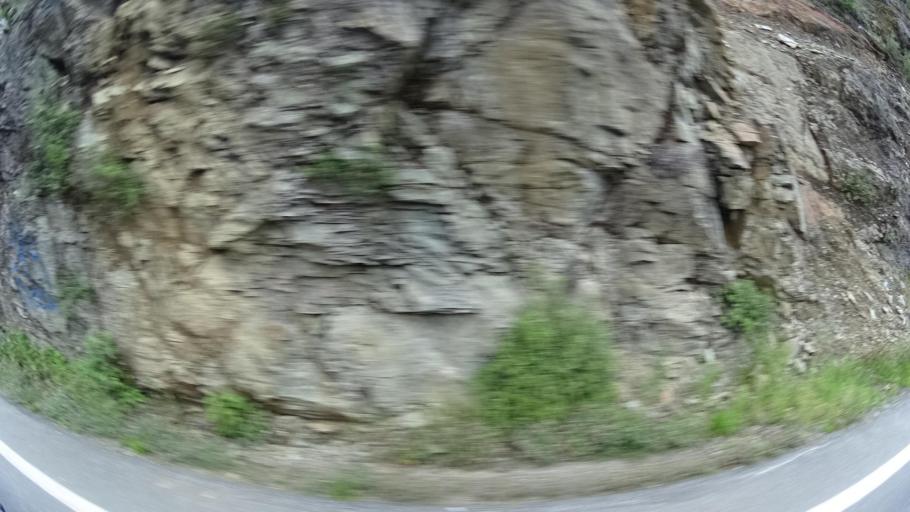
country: US
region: California
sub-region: Humboldt County
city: Willow Creek
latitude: 41.1154
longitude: -123.6881
